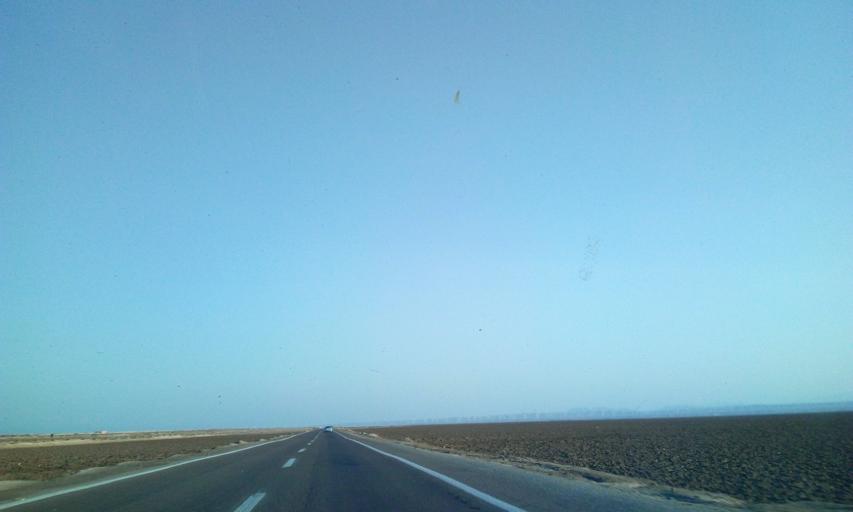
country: EG
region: South Sinai
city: Tor
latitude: 28.2630
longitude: 33.1513
